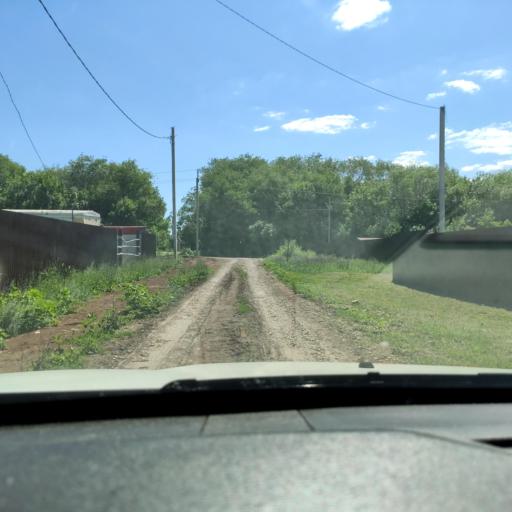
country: RU
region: Samara
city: Dubovyy Umet
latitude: 53.0322
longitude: 50.2484
